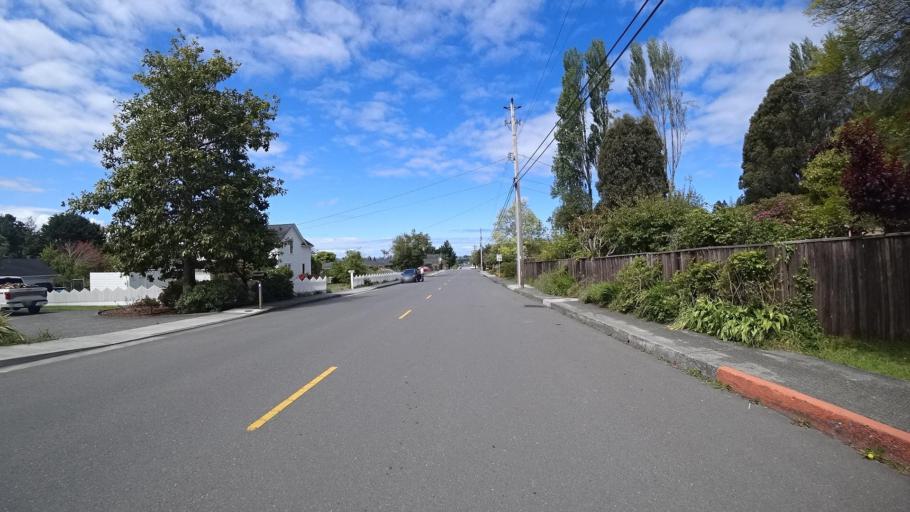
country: US
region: California
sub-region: Humboldt County
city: Bayside
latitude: 40.8573
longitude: -124.0628
